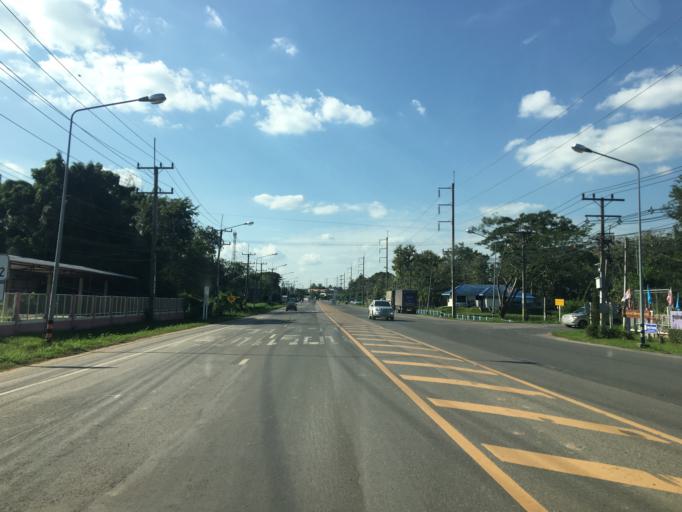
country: TH
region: Phayao
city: Chun
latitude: 19.3364
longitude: 100.1336
